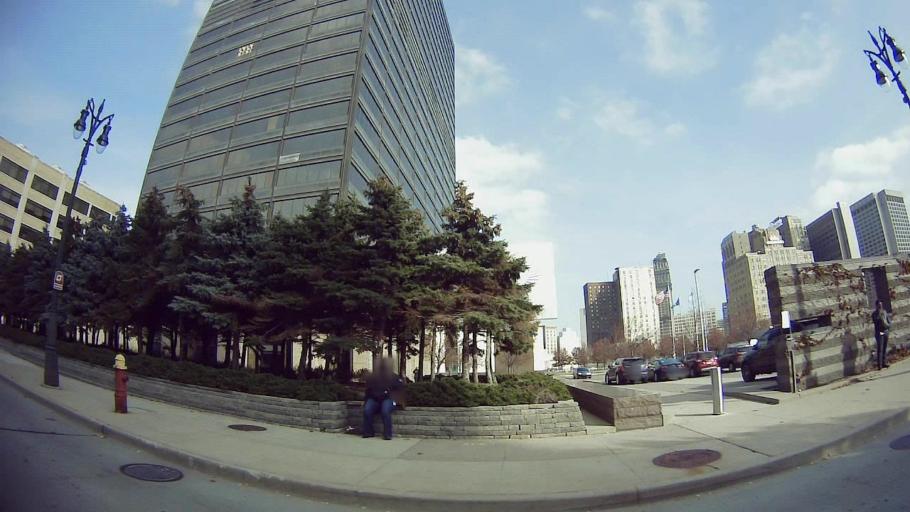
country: US
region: Michigan
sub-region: Wayne County
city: Detroit
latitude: 42.3332
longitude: -83.0583
